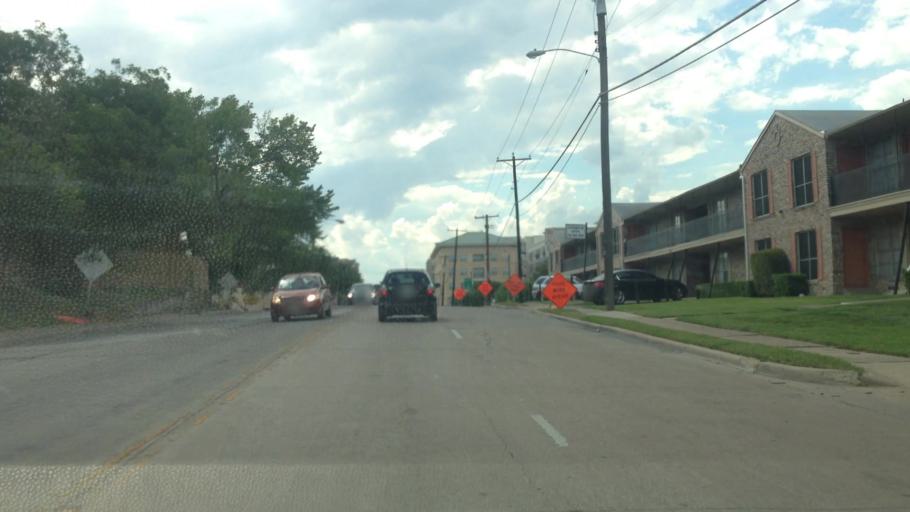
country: US
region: Texas
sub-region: Dallas County
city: Dallas
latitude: 32.7495
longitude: -96.8206
